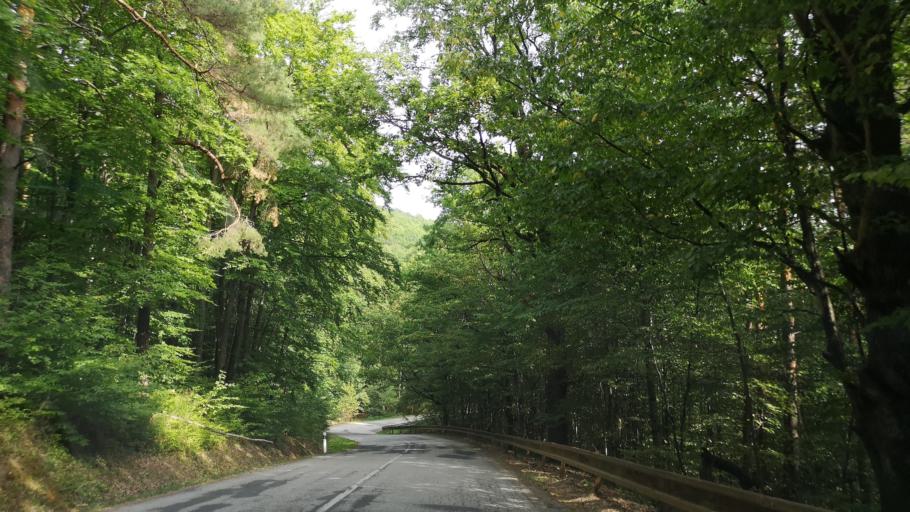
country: SK
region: Banskobystricky
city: Revuca
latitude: 48.6049
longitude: 20.1628
